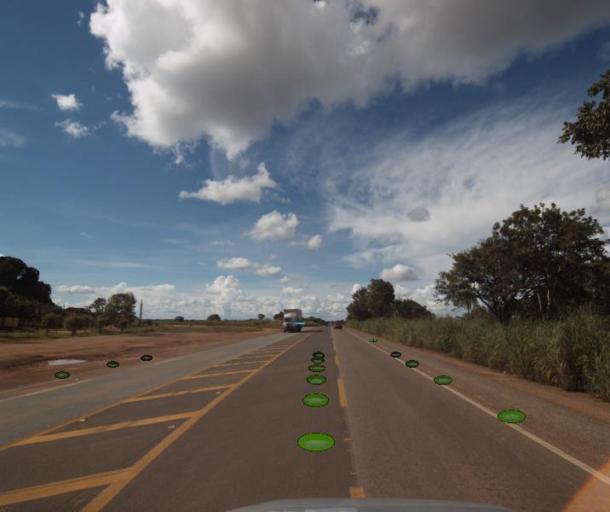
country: BR
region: Goias
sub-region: Porangatu
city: Porangatu
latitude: -13.1037
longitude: -49.1993
